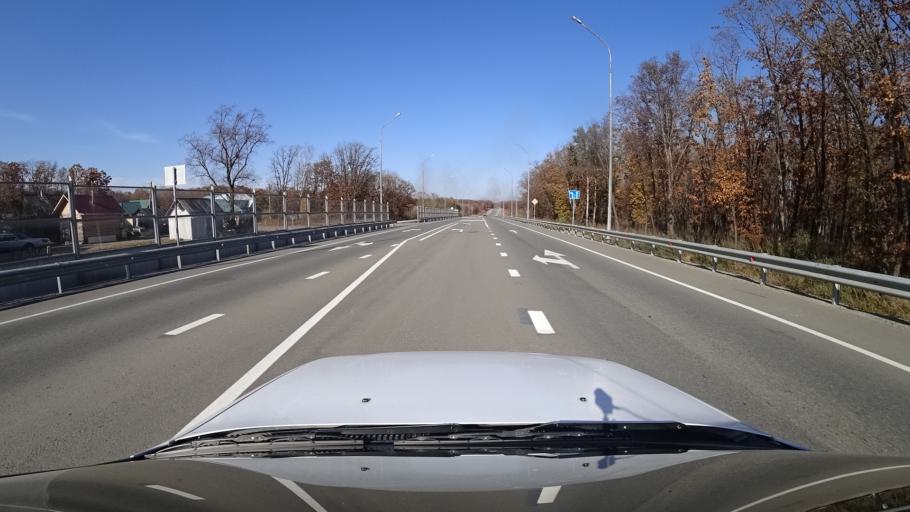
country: RU
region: Primorskiy
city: Dal'nerechensk
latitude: 45.8825
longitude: 133.7293
